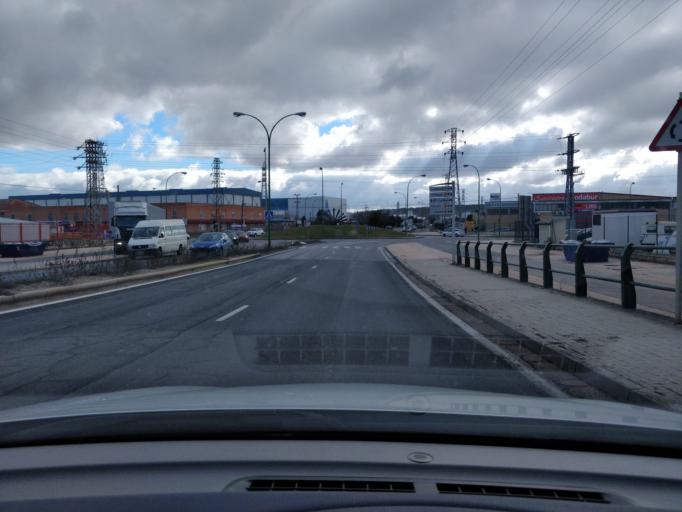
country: ES
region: Castille and Leon
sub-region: Provincia de Burgos
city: Burgos
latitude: 42.3528
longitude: -3.6487
